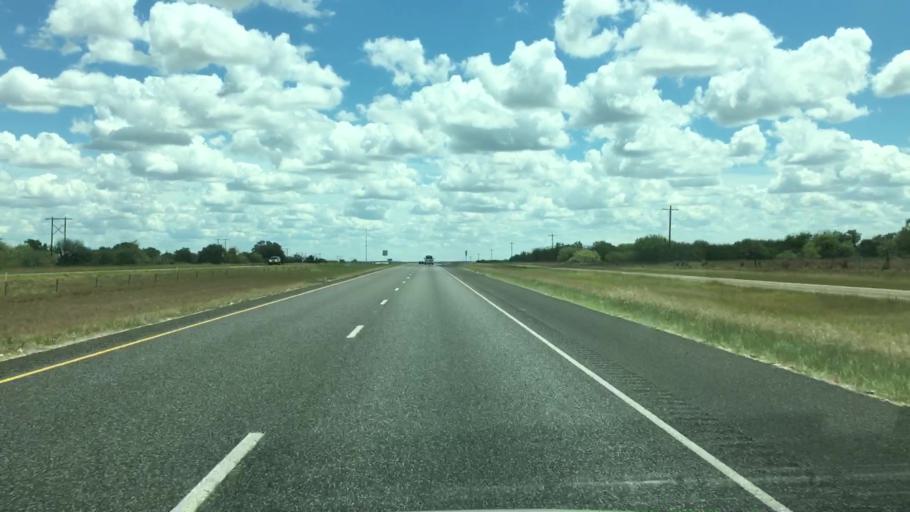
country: US
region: Texas
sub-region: Atascosa County
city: Pleasanton
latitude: 28.8179
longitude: -98.3592
